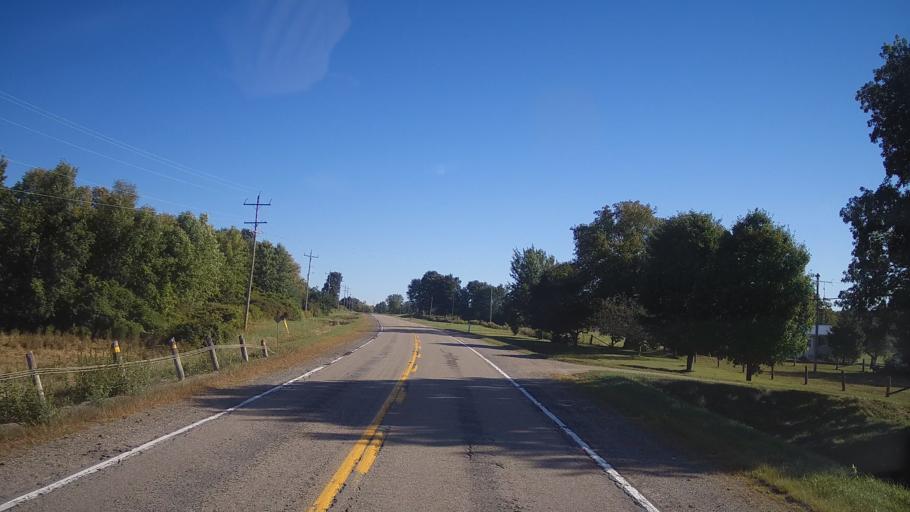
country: CA
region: Ontario
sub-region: Lanark County
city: Smiths Falls
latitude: 44.6179
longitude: -76.0473
